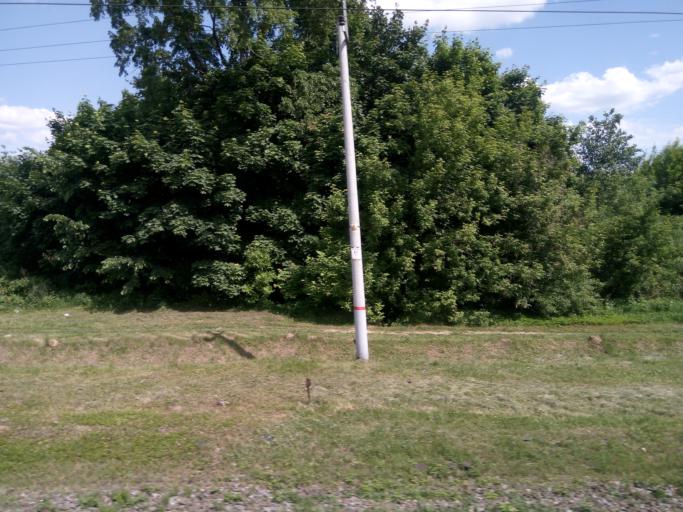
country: RU
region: Moscow
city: Zagor'ye
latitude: 55.5705
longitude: 37.6646
